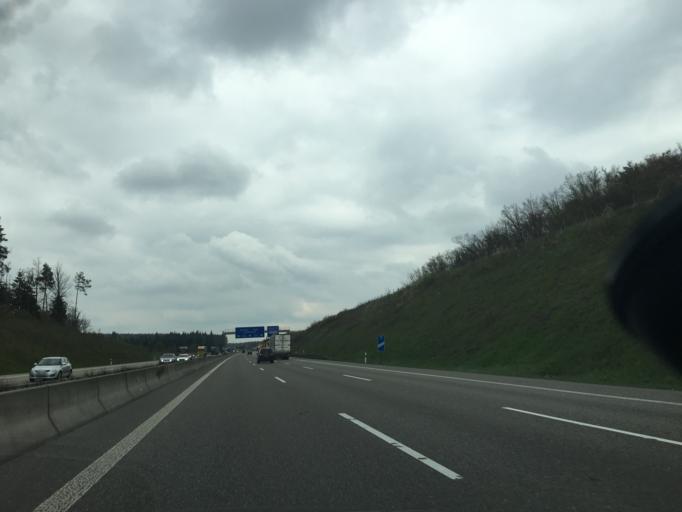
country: DE
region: Baden-Wuerttemberg
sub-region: Karlsruhe Region
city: Wurmberg
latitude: 48.8756
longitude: 8.7890
